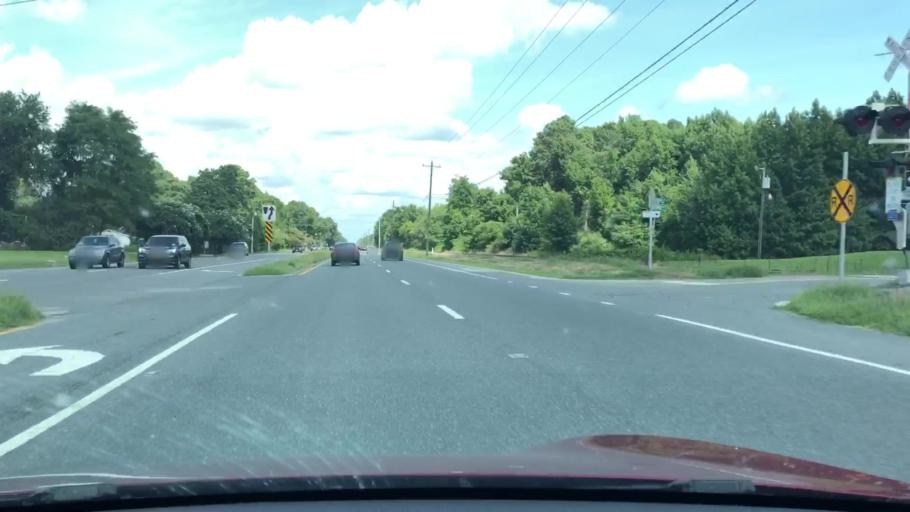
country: US
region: Virginia
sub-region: Northampton County
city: Eastville
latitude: 37.4266
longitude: -75.8905
